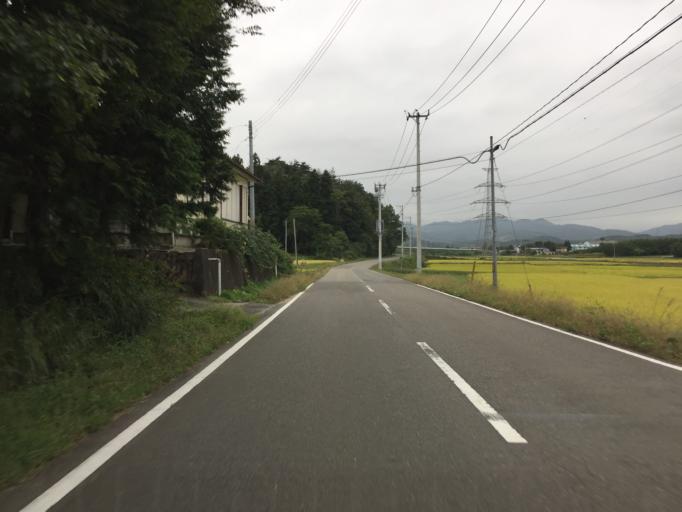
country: JP
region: Fukushima
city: Nihommatsu
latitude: 37.6470
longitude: 140.4702
